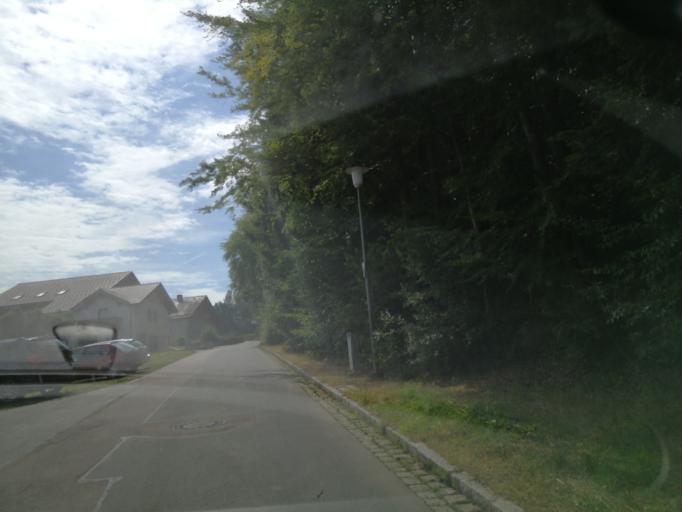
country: DE
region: Bavaria
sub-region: Upper Palatinate
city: Falkenstein
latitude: 49.0928
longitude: 12.4852
